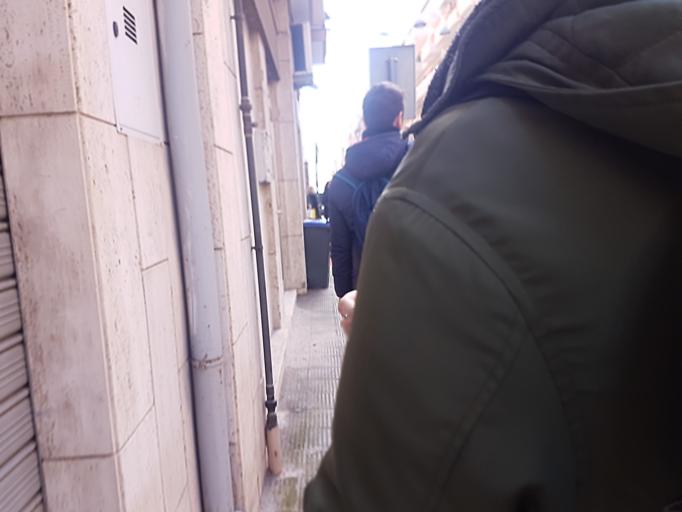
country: IT
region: Apulia
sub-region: Provincia di Barletta - Andria - Trani
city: Andria
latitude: 41.2308
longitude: 16.2988
